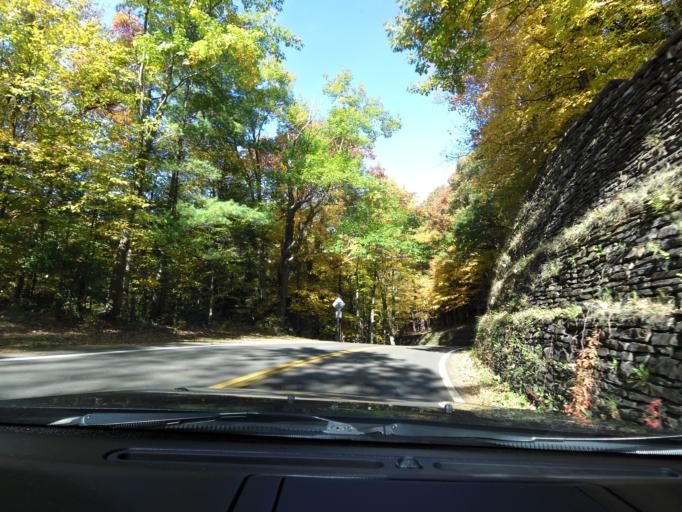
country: US
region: New York
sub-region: Wyoming County
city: Castile
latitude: 42.6138
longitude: -78.0098
